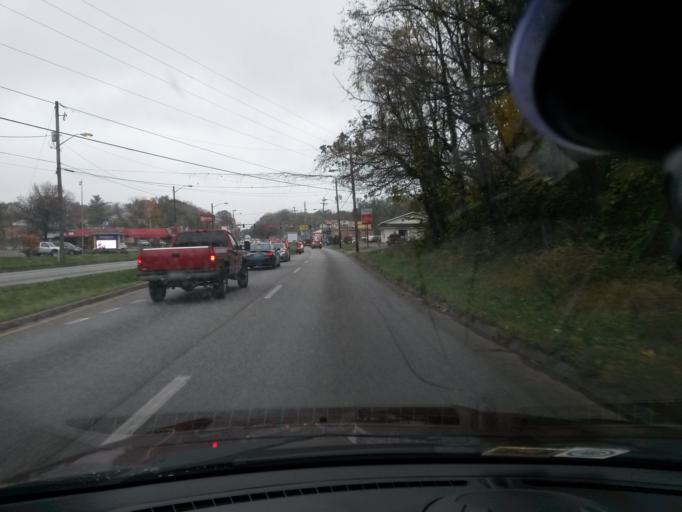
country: US
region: Virginia
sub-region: Roanoke County
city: Vinton
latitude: 37.2917
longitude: -79.9081
